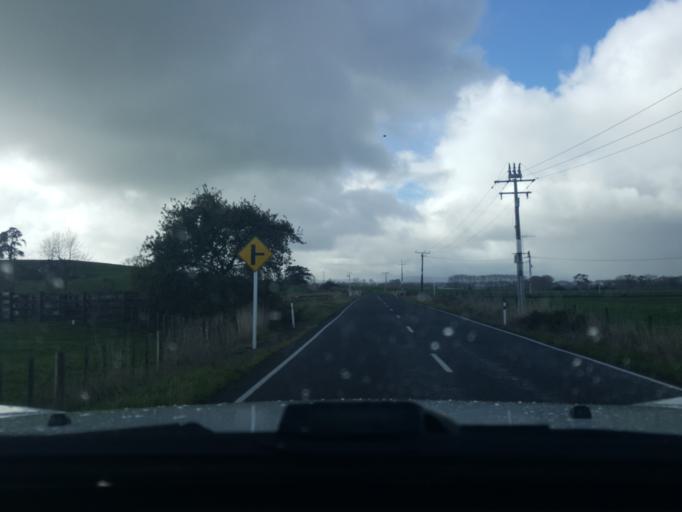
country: NZ
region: Waikato
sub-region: Waikato District
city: Te Kauwhata
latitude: -37.4489
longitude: 175.1007
